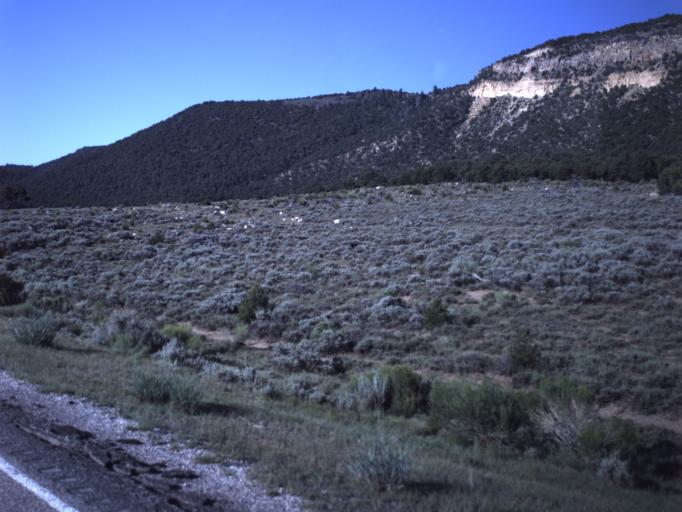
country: US
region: Utah
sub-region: Wayne County
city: Loa
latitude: 38.7119
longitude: -111.4033
